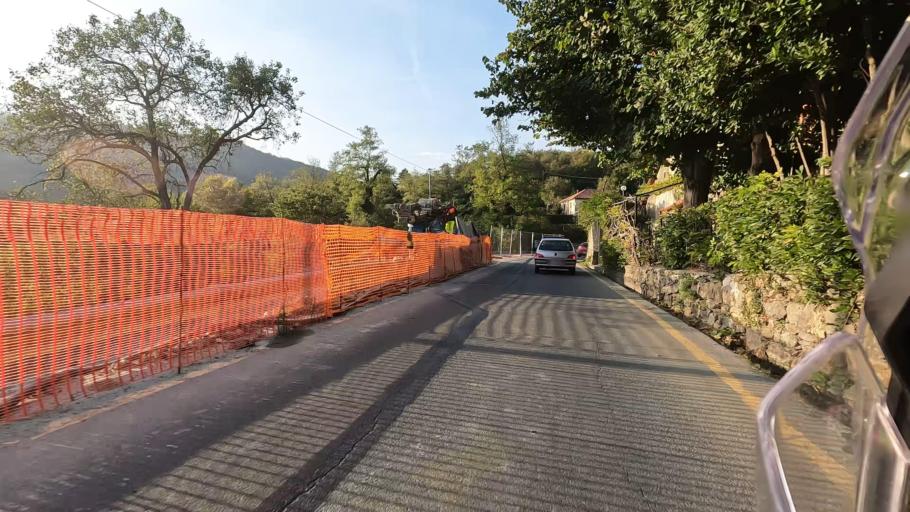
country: IT
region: Liguria
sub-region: Provincia di Savona
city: San Giovanni
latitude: 44.4076
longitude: 8.4888
